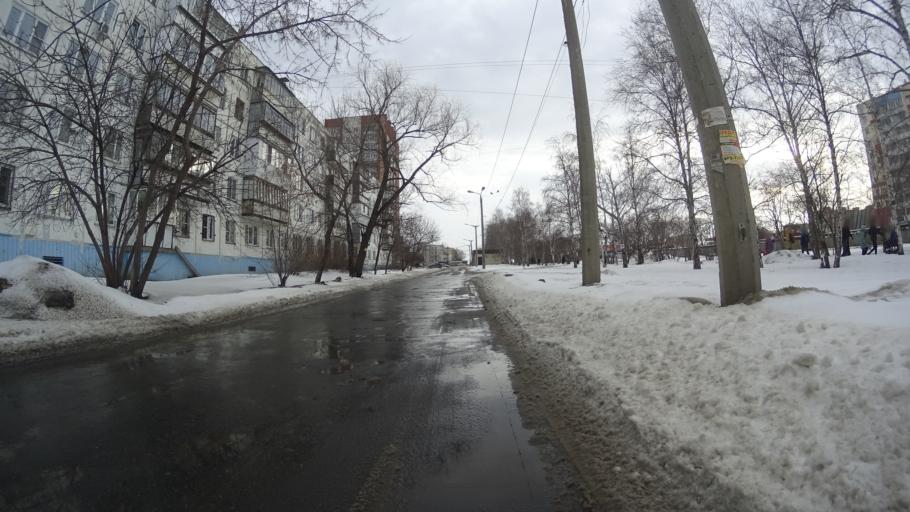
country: RU
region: Chelyabinsk
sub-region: Gorod Chelyabinsk
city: Chelyabinsk
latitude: 55.1962
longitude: 61.3223
